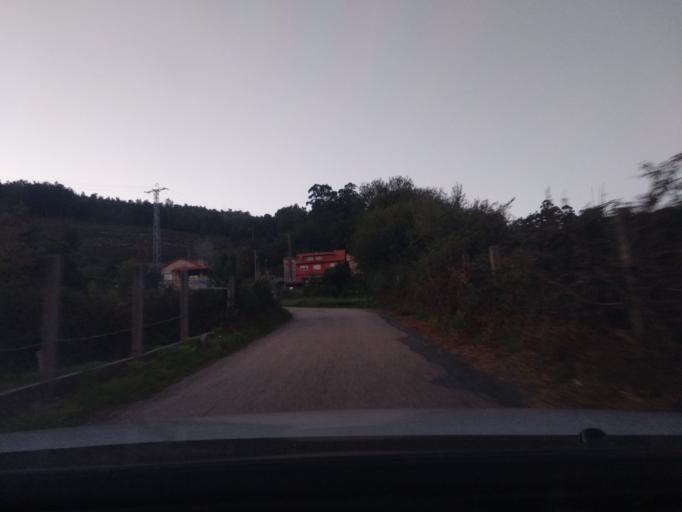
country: ES
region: Galicia
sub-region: Provincia de Pontevedra
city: Moana
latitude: 42.3055
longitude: -8.6972
